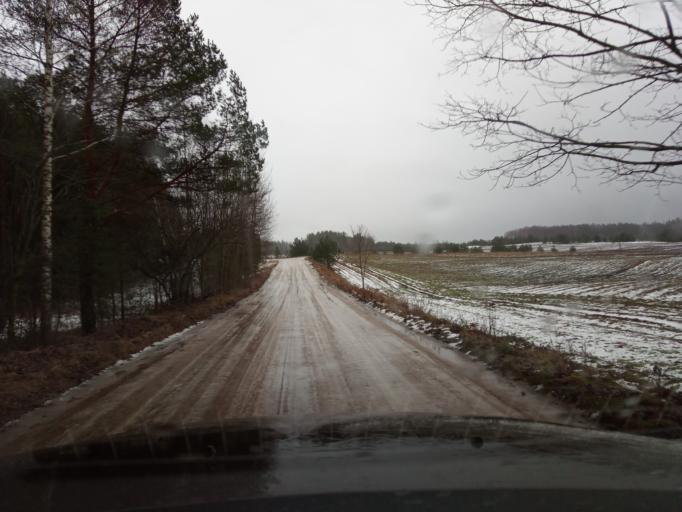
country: LT
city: Svencioneliai
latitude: 55.3442
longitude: 25.8388
